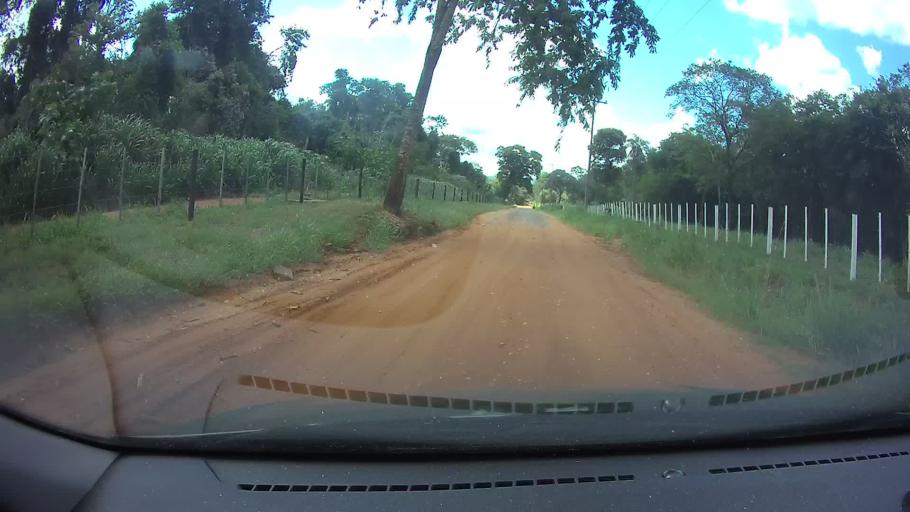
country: PY
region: Paraguari
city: La Colmena
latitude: -25.9205
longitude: -56.7940
